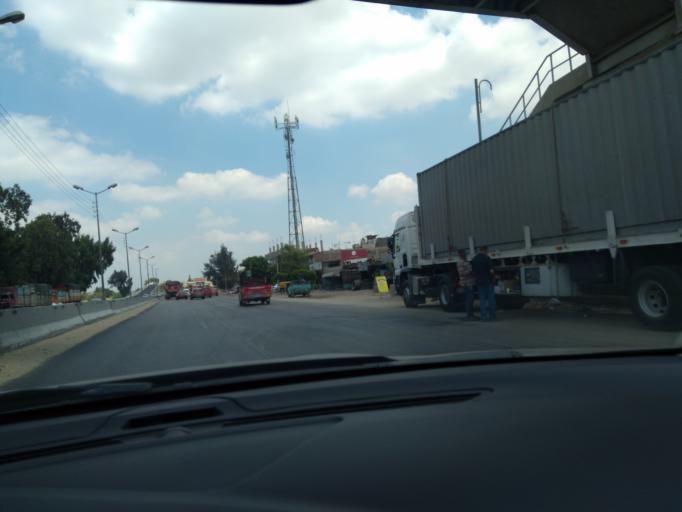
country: EG
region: Al Isma'iliyah
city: Ismailia
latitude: 30.6743
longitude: 32.2711
